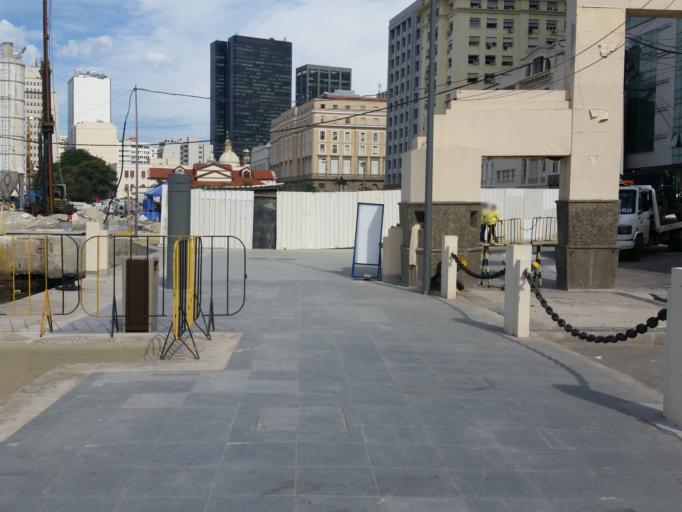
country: BR
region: Rio de Janeiro
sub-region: Rio De Janeiro
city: Rio de Janeiro
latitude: -22.8985
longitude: -43.1766
